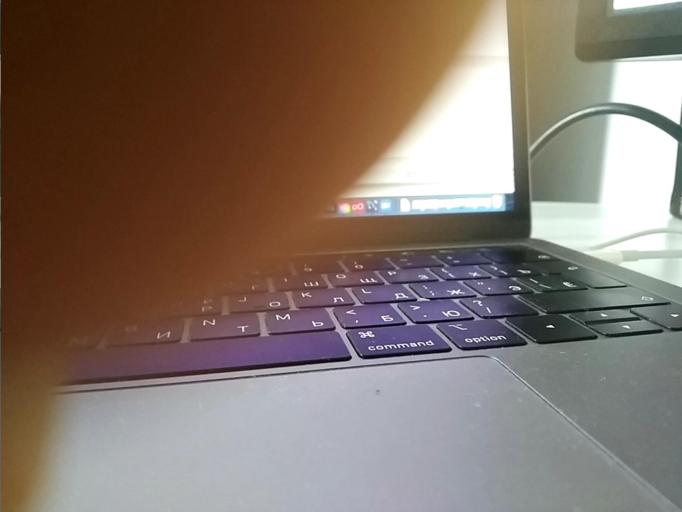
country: RU
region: Moskovskaya
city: Balashikha
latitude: 55.8023
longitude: 37.9631
